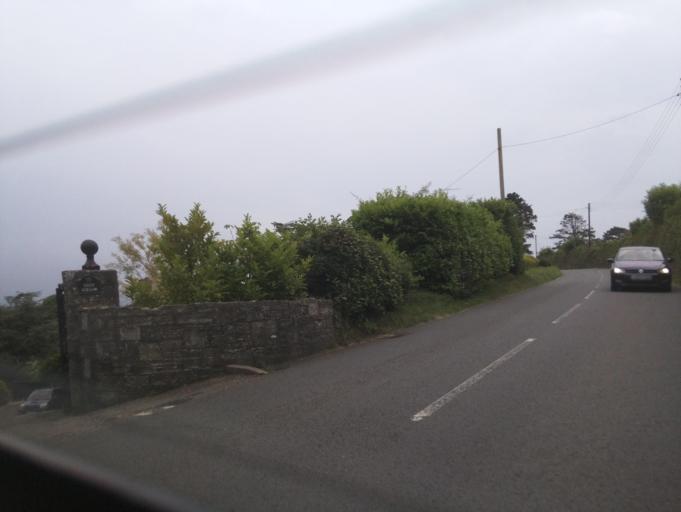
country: GB
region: England
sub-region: Devon
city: Colyton
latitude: 50.7013
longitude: -3.0892
